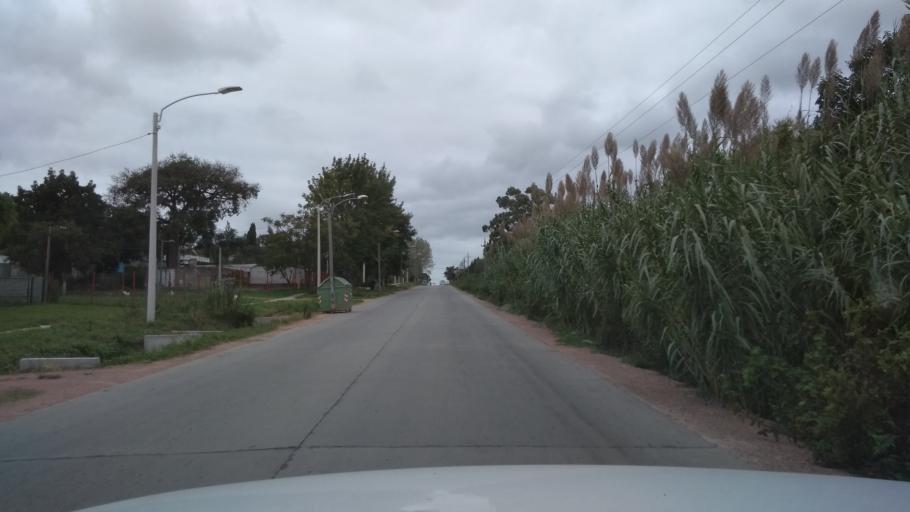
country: UY
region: Canelones
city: Toledo
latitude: -34.7852
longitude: -56.1405
